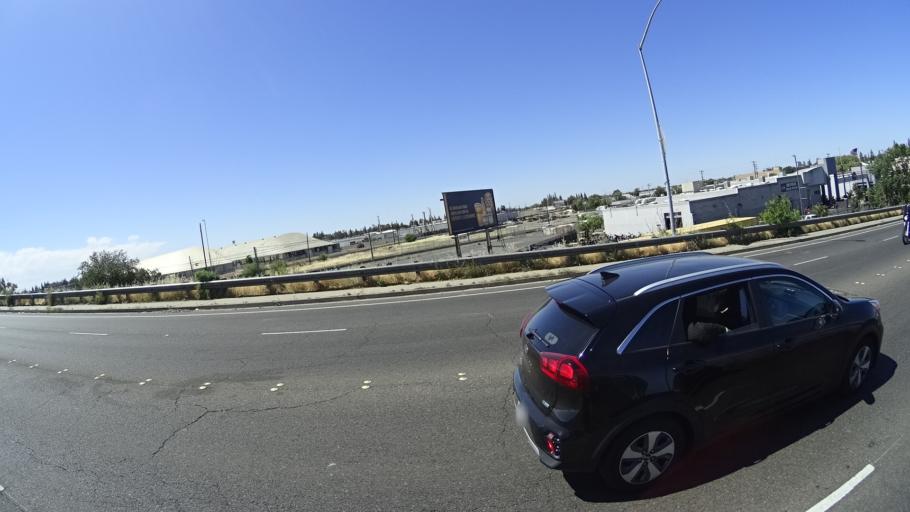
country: US
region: California
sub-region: Sacramento County
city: Sacramento
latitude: 38.6064
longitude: -121.4421
